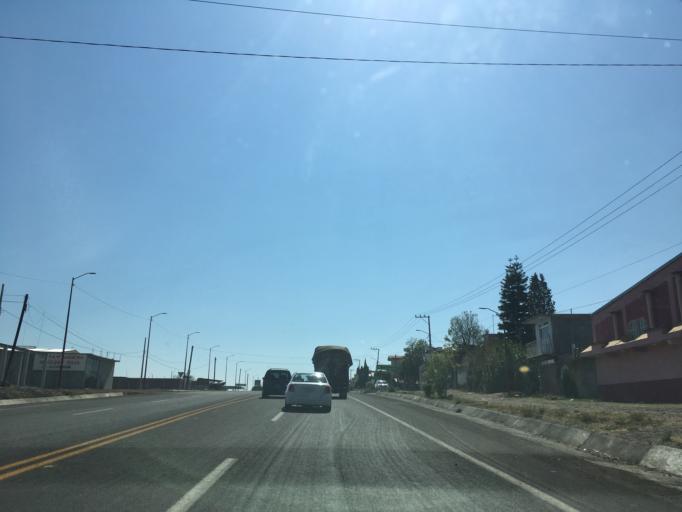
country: MX
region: Michoacan
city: Indaparapeo
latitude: 19.7911
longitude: -100.9733
